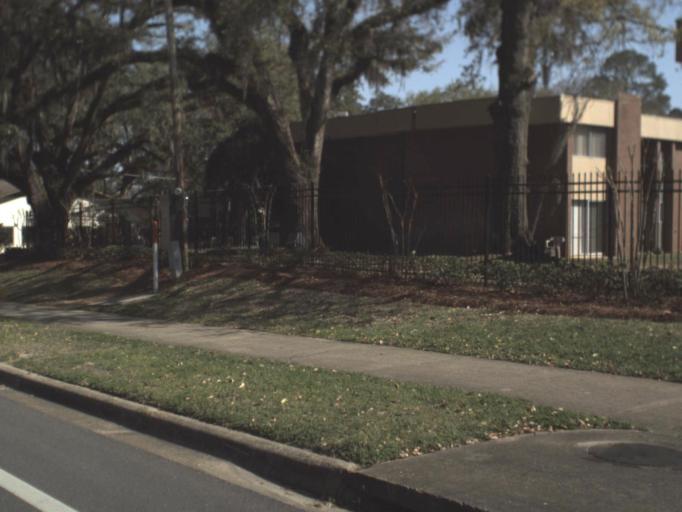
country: US
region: Florida
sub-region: Leon County
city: Tallahassee
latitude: 30.4402
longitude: -84.3099
